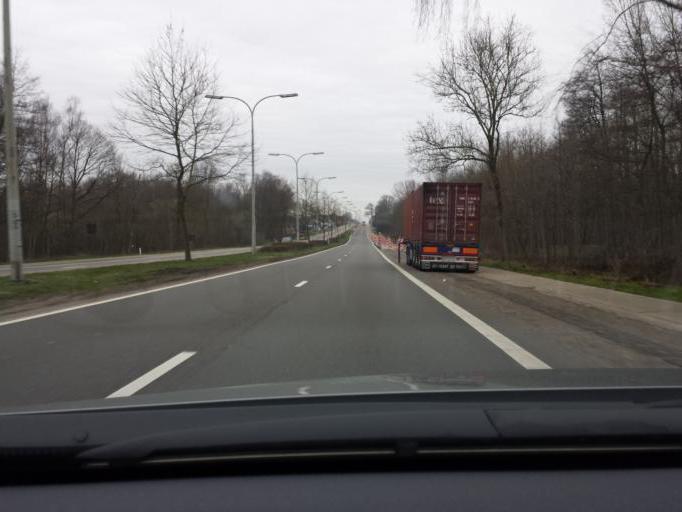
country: BE
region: Flanders
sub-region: Provincie Limburg
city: Helchteren
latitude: 51.0484
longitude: 5.3810
